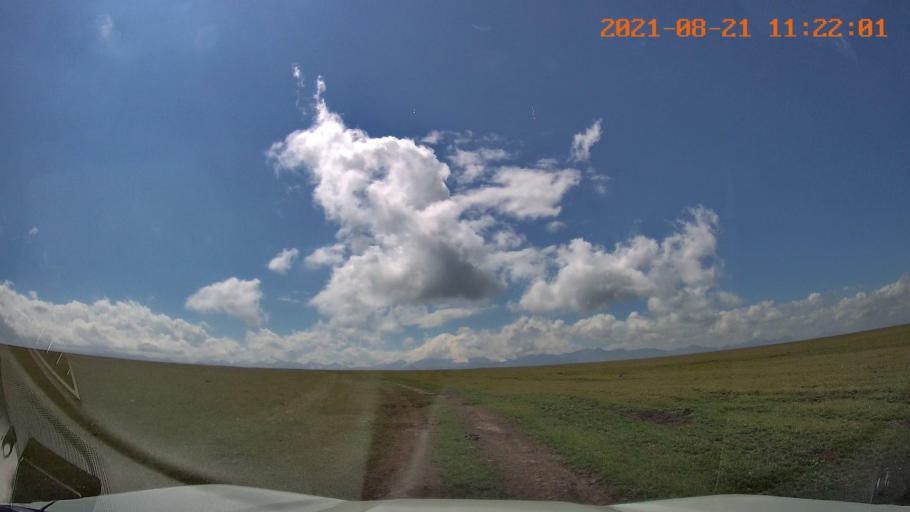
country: RU
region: Stavropol'skiy
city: Kislovodsk
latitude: 43.6165
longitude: 42.5922
